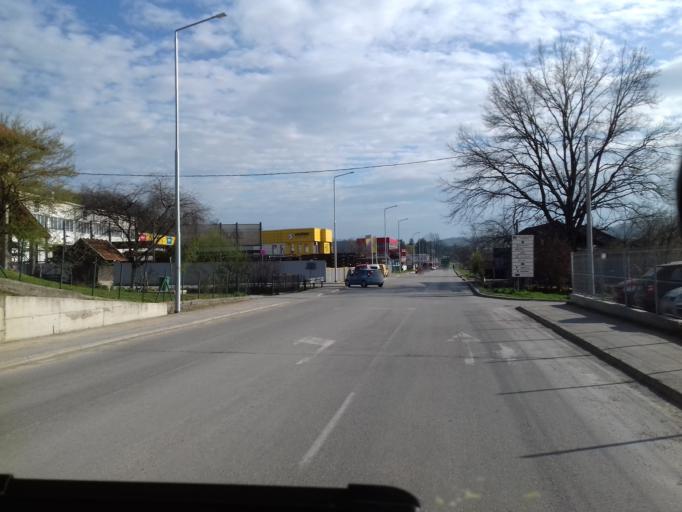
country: BA
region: Federation of Bosnia and Herzegovina
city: Tesanj
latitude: 44.6284
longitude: 18.0012
